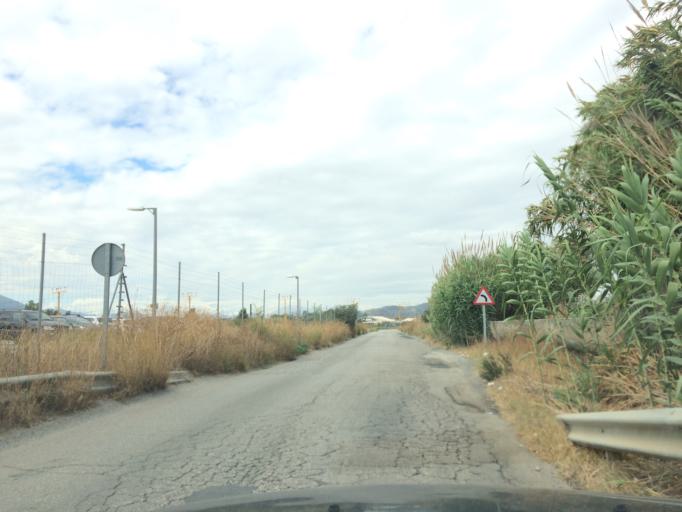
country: ES
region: Andalusia
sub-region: Provincia de Malaga
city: Alhaurin de la Torre
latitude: 36.6873
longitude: -4.5146
